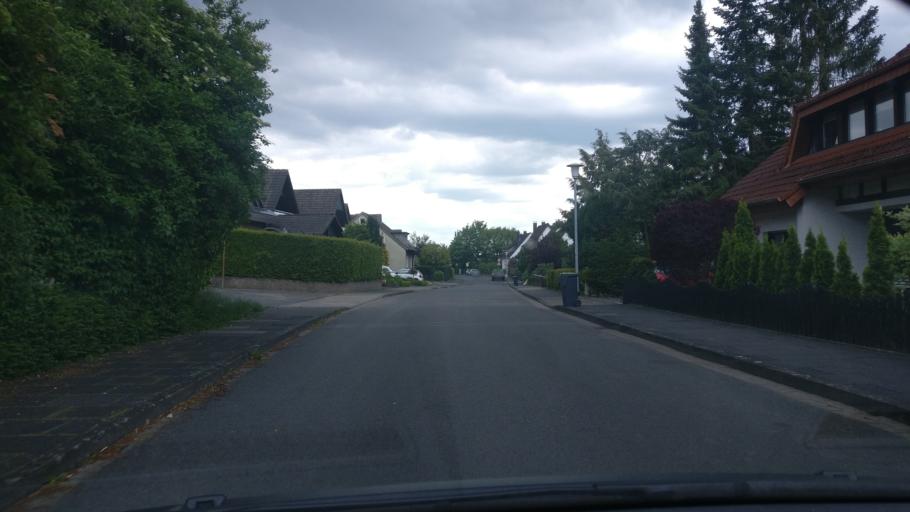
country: DE
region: North Rhine-Westphalia
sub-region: Regierungsbezirk Detmold
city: Lage
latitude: 51.9985
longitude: 8.7969
